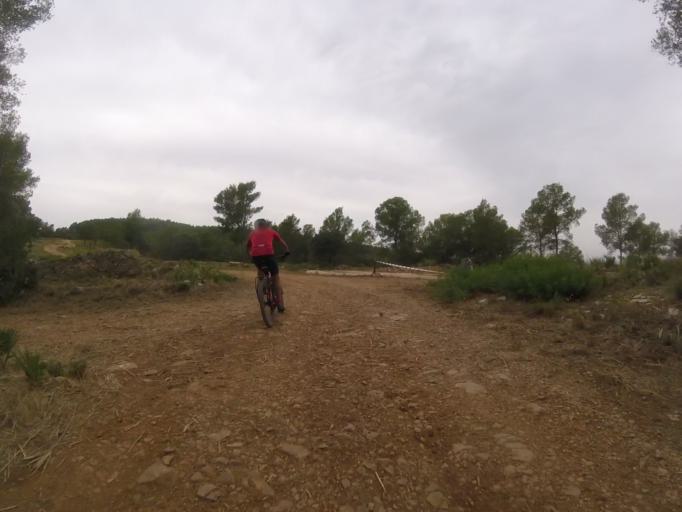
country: ES
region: Valencia
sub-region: Provincia de Castello
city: Alcala de Xivert
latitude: 40.3175
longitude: 0.2701
